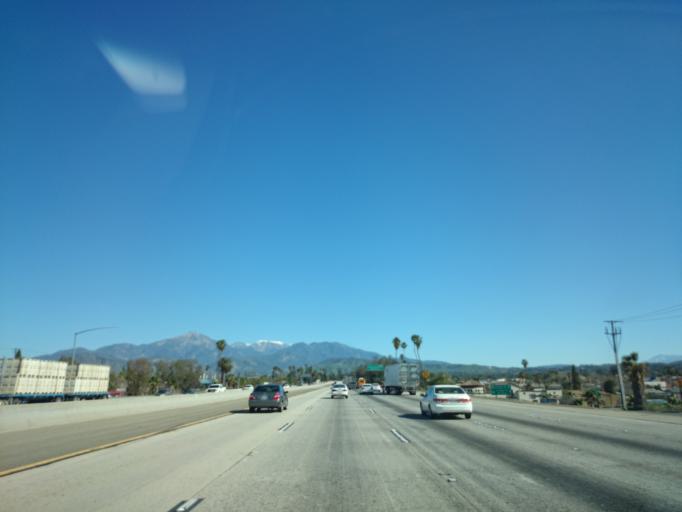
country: US
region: California
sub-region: San Bernardino County
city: Redlands
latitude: 34.0617
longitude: -117.1890
